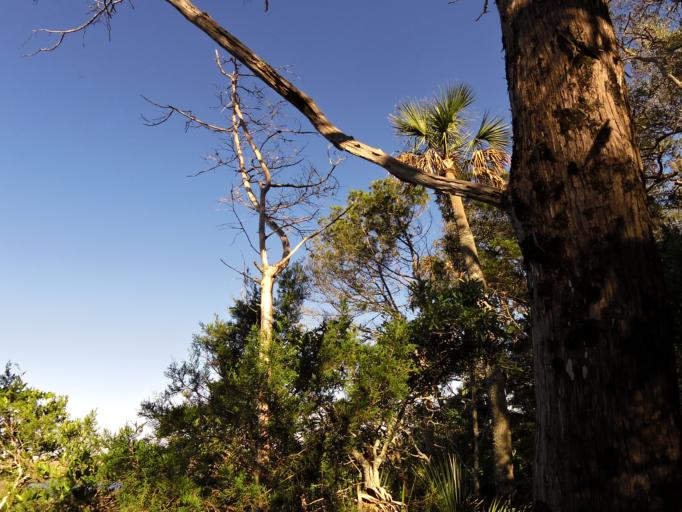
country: US
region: Florida
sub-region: Saint Johns County
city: Saint Augustine Shores
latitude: 29.7379
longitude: -81.4317
